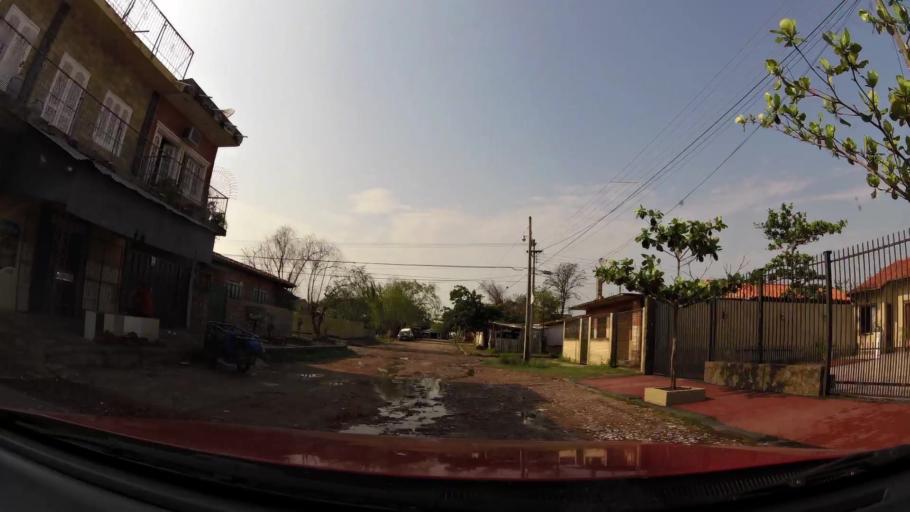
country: PY
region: Asuncion
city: Asuncion
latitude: -25.2979
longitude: -57.6663
